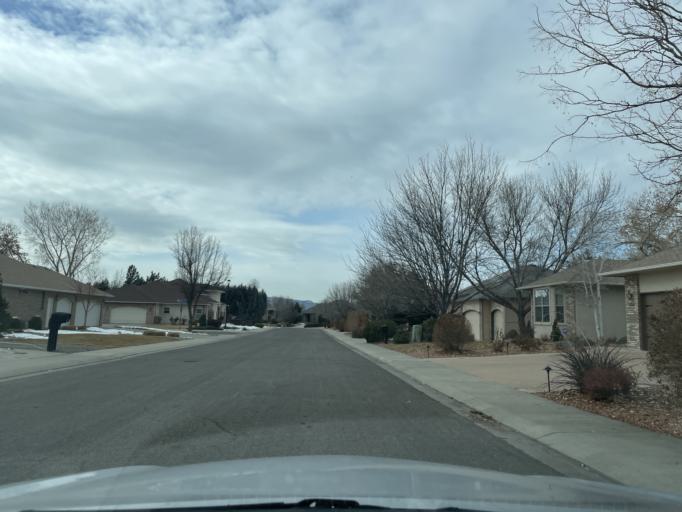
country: US
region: Colorado
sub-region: Mesa County
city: Grand Junction
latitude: 39.1051
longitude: -108.5827
